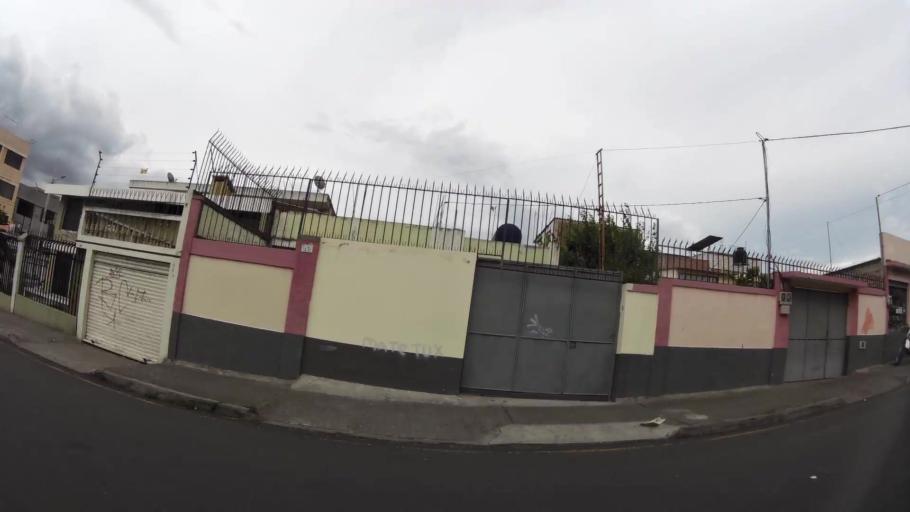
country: EC
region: Tungurahua
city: Ambato
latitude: -1.2522
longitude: -78.6303
